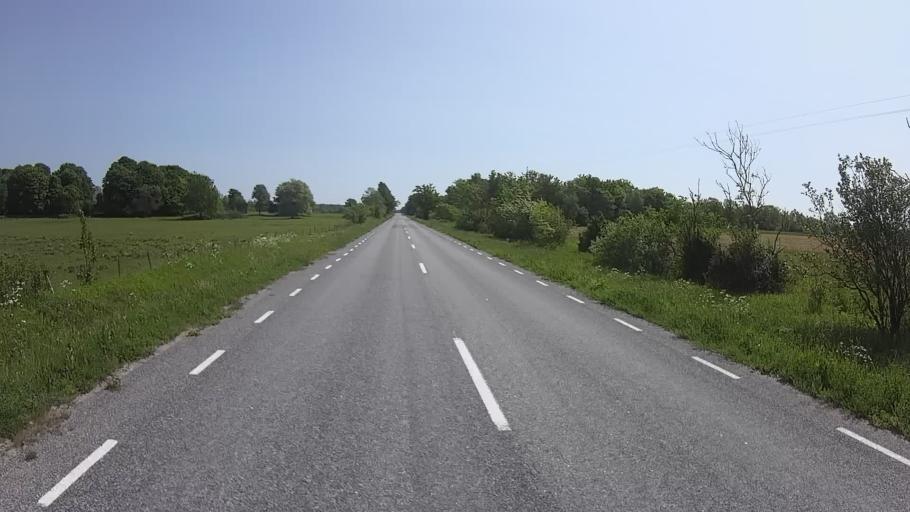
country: EE
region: Saare
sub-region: Kuressaare linn
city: Kuressaare
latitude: 58.3688
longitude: 22.0491
